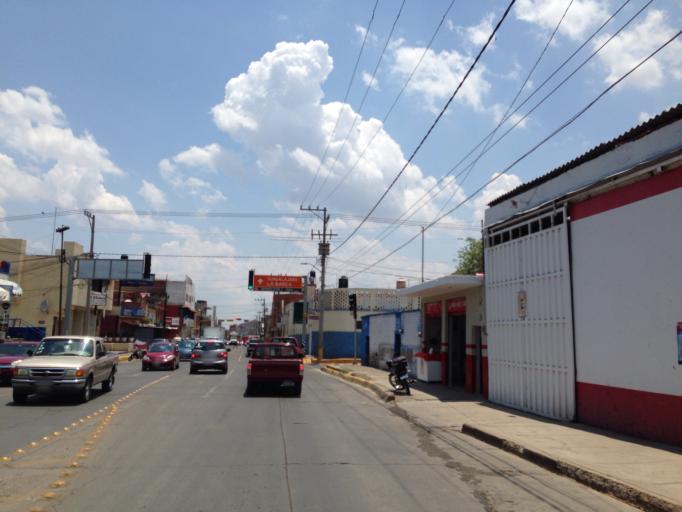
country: MX
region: Jalisco
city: Atotonilco el Alto
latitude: 20.5490
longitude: -102.5061
